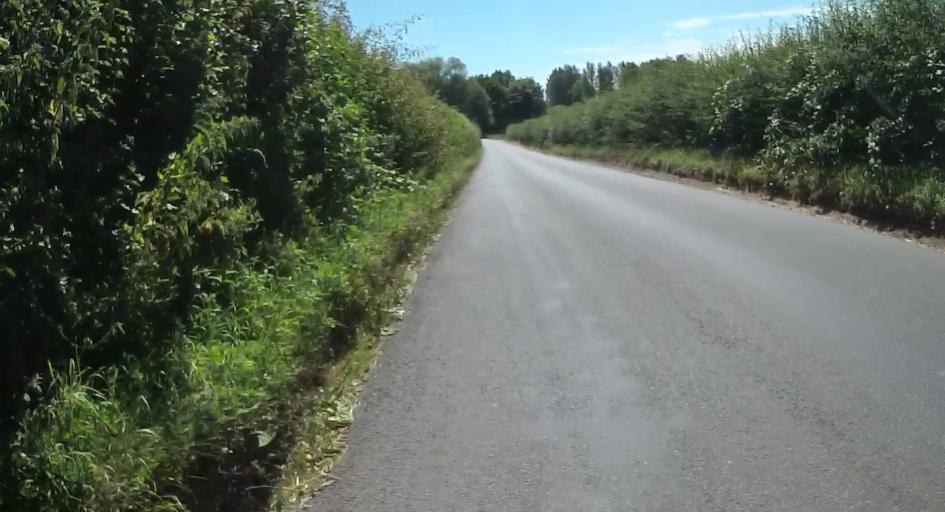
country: GB
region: England
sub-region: Hampshire
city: Kings Worthy
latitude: 51.0912
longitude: -1.2717
